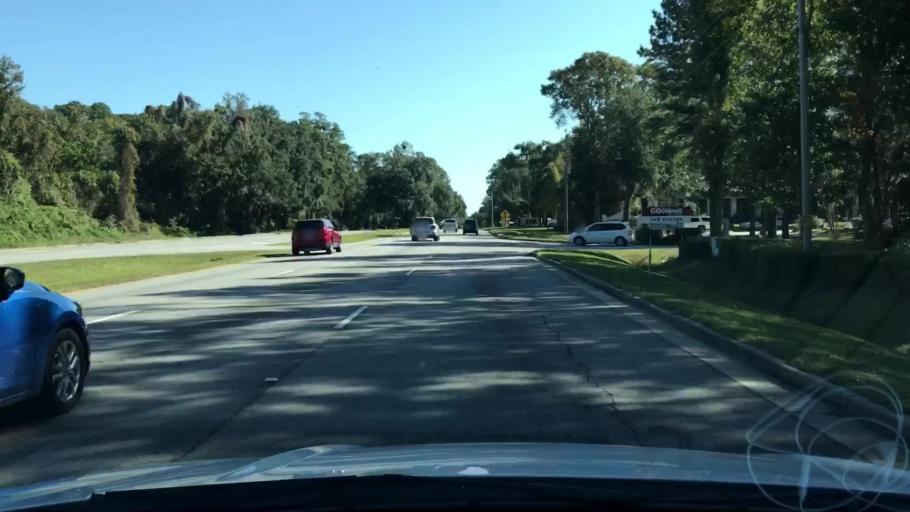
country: US
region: South Carolina
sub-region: Beaufort County
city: Bluffton
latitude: 32.2398
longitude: -80.8142
